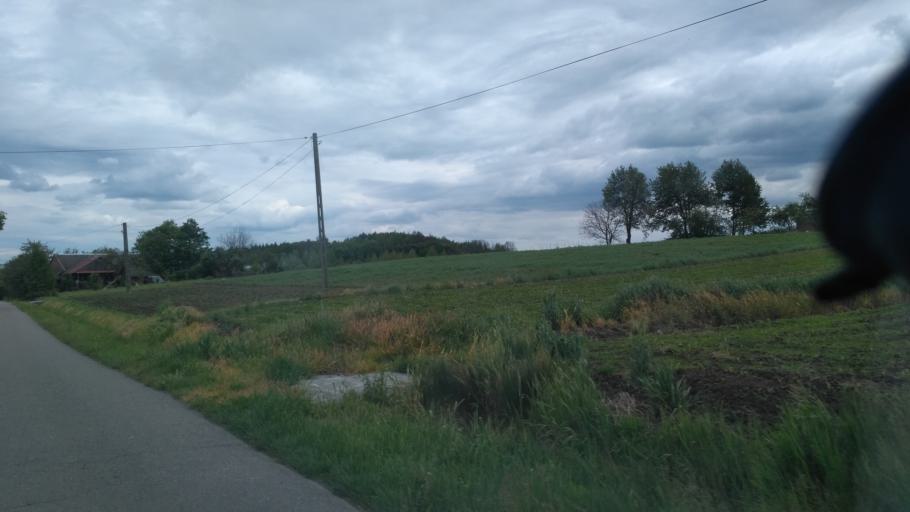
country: PL
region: Subcarpathian Voivodeship
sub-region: Powiat przeworski
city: Jawornik Polski
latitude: 49.8355
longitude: 22.3032
